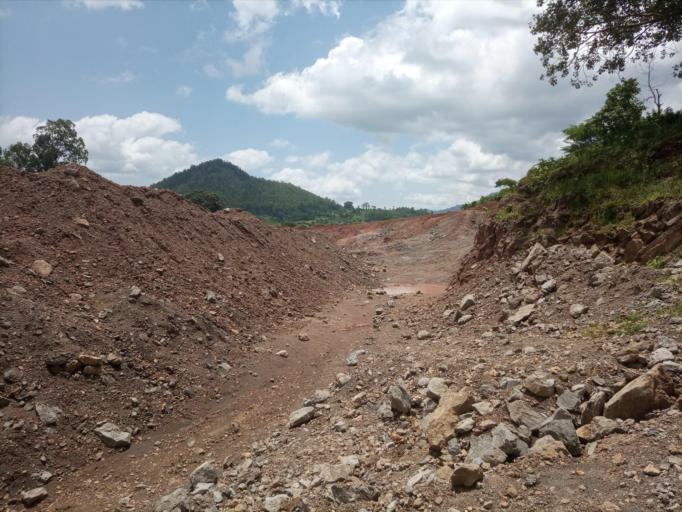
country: ET
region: Southern Nations, Nationalities, and People's Region
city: K'olito
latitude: 7.3039
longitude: 37.9784
